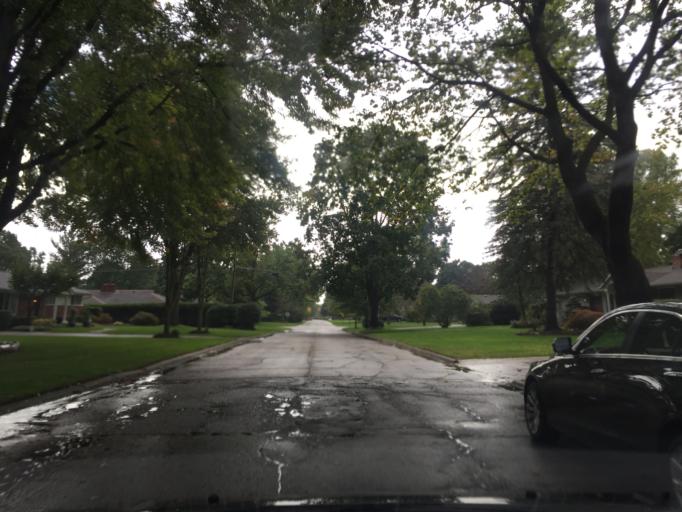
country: US
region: Michigan
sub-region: Oakland County
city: Bingham Farms
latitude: 42.5415
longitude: -83.2625
